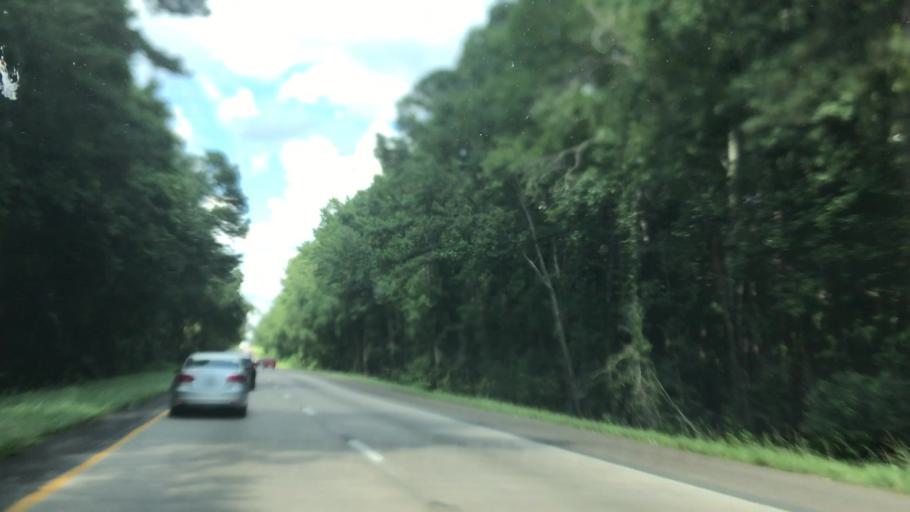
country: US
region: South Carolina
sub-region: Hampton County
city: Yemassee
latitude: 32.7389
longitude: -80.8404
